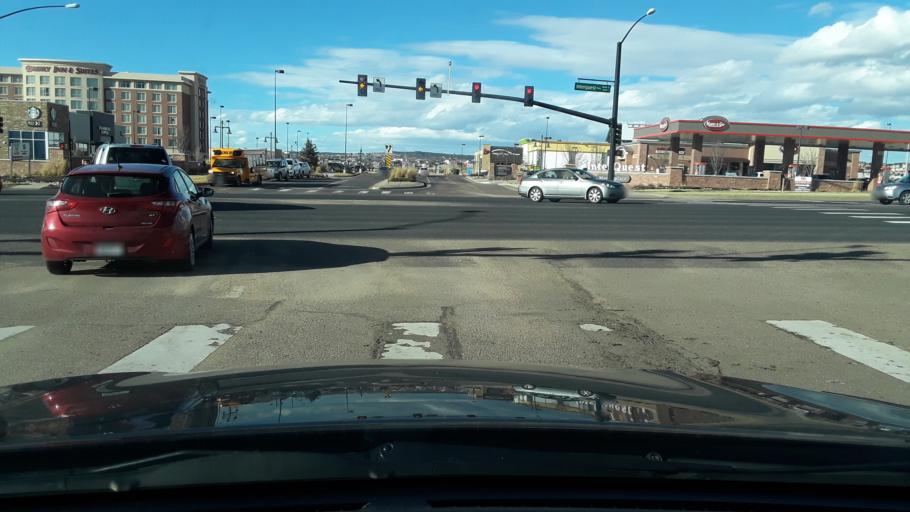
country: US
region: Colorado
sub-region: El Paso County
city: Air Force Academy
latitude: 38.9906
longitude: -104.8077
